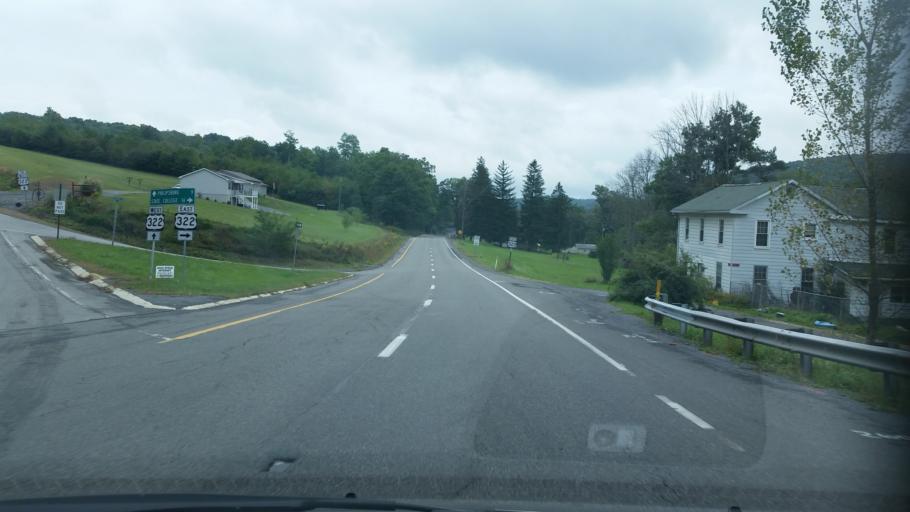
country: US
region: Pennsylvania
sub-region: Centre County
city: Stormstown
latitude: 40.8248
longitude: -78.1061
